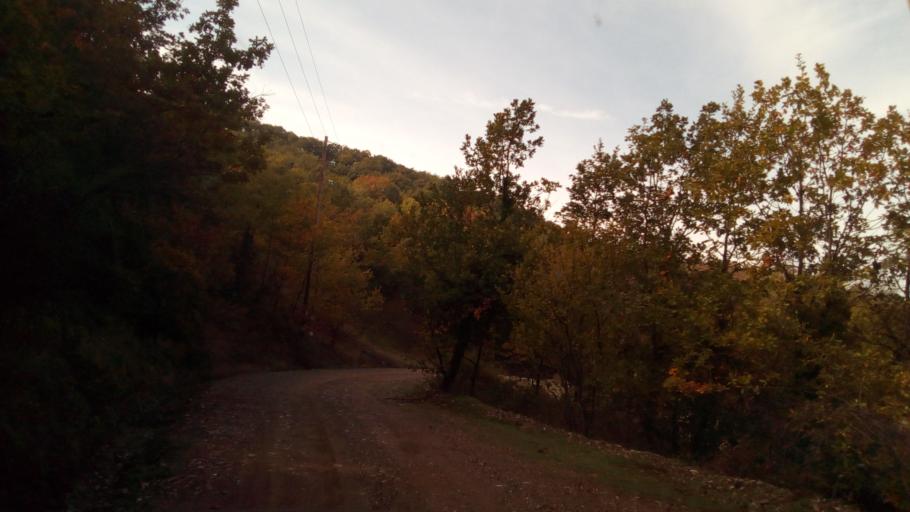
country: GR
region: West Greece
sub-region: Nomos Achaias
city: Kamarai
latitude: 38.4747
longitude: 22.0234
